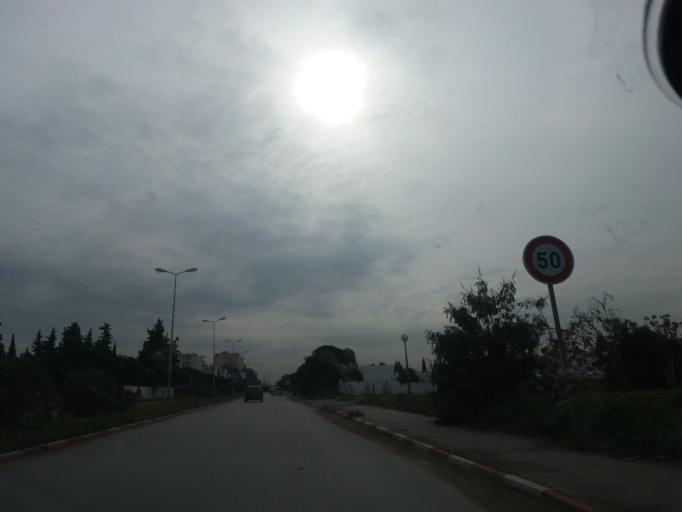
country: TN
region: Tunis
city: Tunis
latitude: 36.8496
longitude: 10.1562
